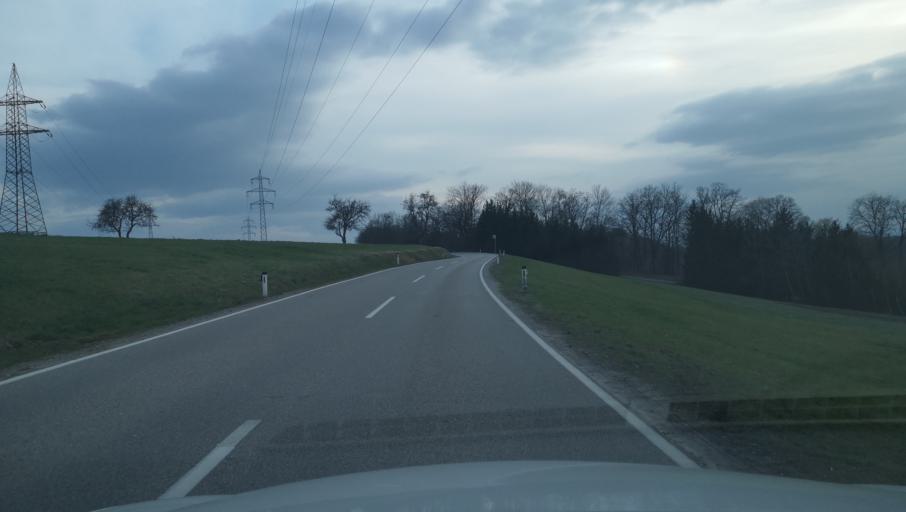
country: AT
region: Lower Austria
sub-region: Politischer Bezirk Amstetten
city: Winklarn
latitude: 48.0893
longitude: 14.8436
